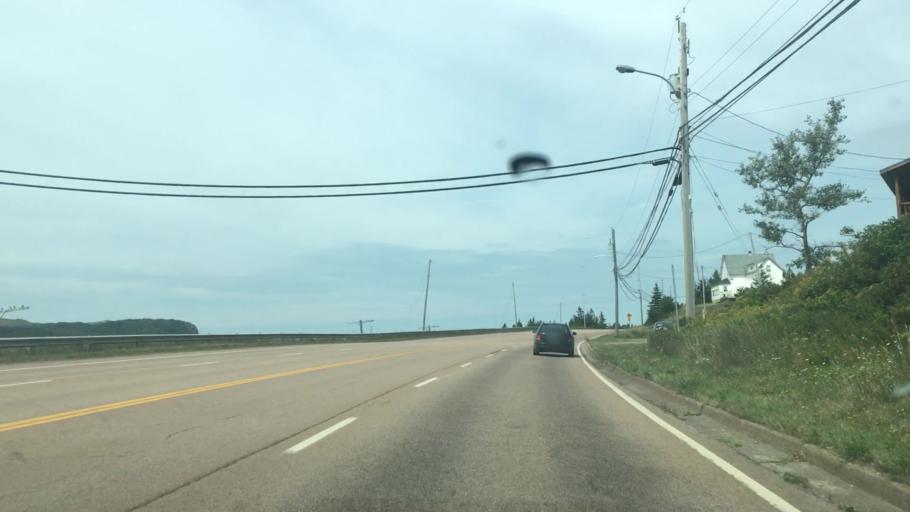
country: CA
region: Nova Scotia
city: Port Hawkesbury
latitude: 45.6266
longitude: -61.3718
